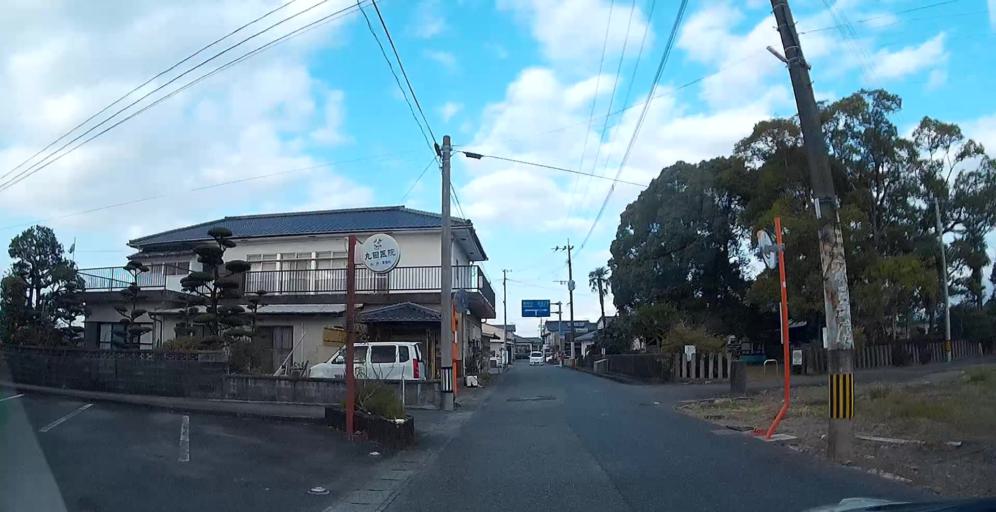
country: JP
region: Kumamoto
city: Yatsushiro
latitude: 32.5345
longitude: 130.6462
